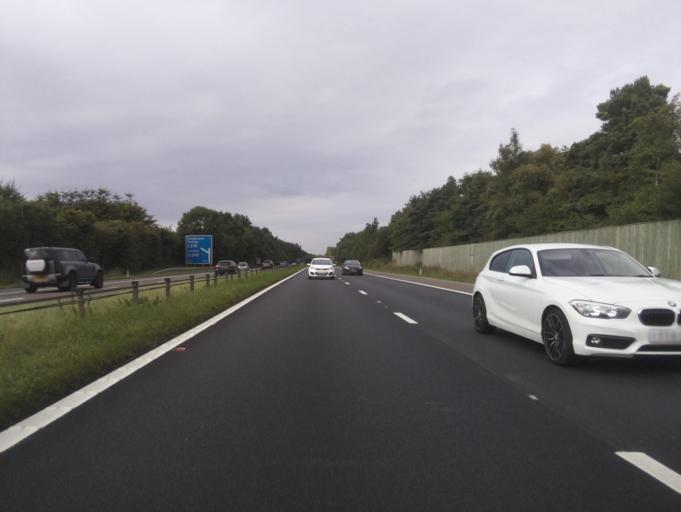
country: GB
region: England
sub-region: County Durham
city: Durham
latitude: 54.7813
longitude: -1.5331
